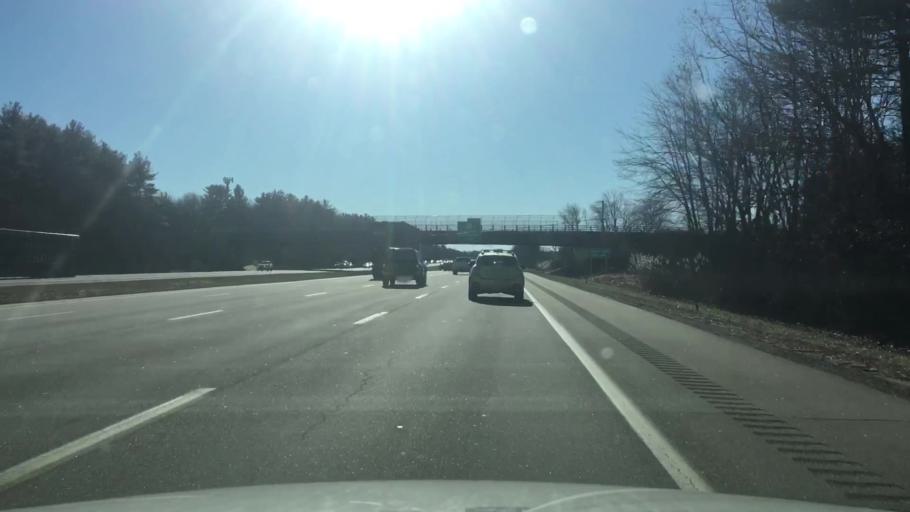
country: US
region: New Hampshire
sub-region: Rockingham County
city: North Hampton
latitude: 42.9858
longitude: -70.8519
